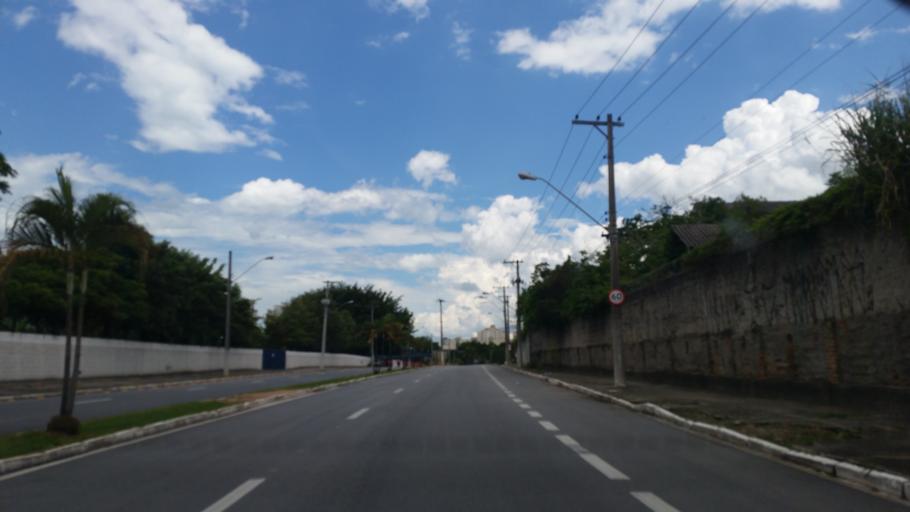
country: BR
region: Sao Paulo
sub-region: Taubate
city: Taubate
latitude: -23.0191
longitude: -45.5829
